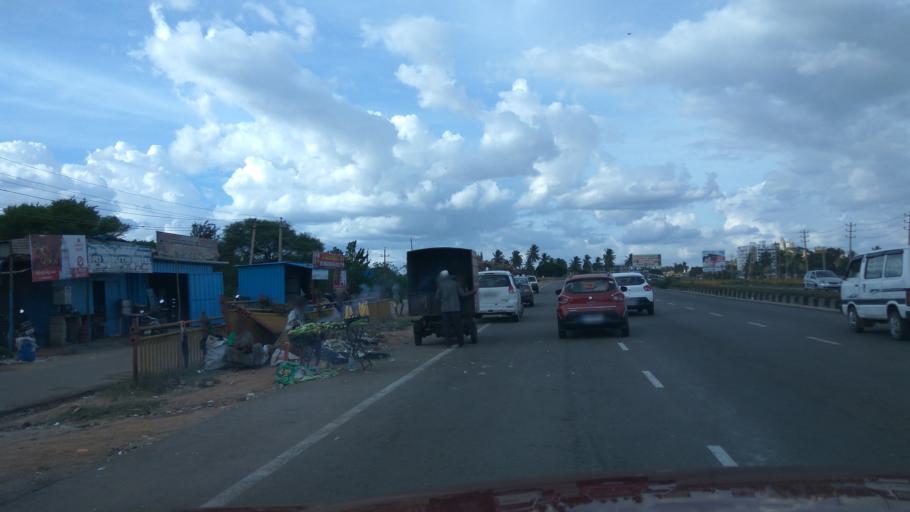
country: IN
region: Karnataka
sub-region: Bangalore Rural
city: Devanhalli
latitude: 13.2507
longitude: 77.7070
